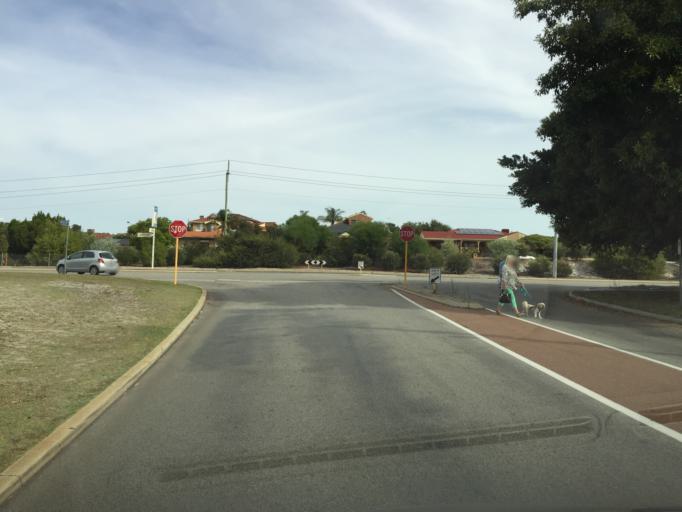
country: AU
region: Western Australia
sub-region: Canning
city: Willetton
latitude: -32.0665
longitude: 115.8784
